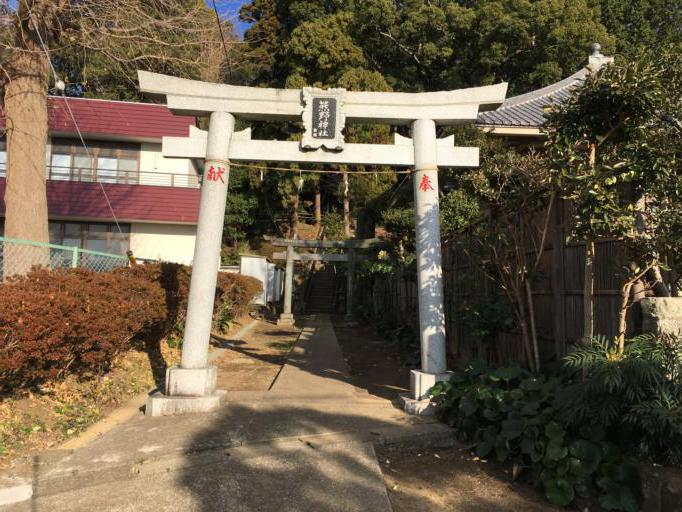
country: JP
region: Kanagawa
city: Kamakura
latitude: 35.3462
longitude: 139.5454
